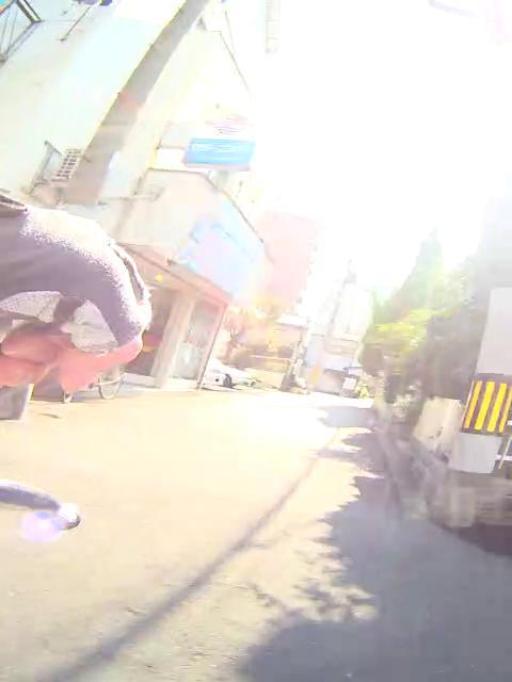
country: JP
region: Osaka
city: Suita
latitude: 34.7370
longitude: 135.5009
